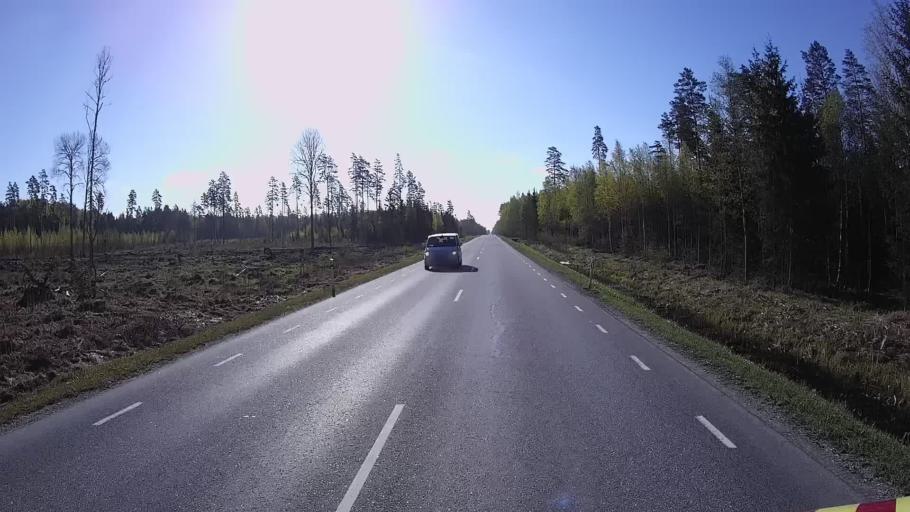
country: EE
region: Paernumaa
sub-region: Vaendra vald (alev)
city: Vandra
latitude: 58.8177
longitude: 25.1602
